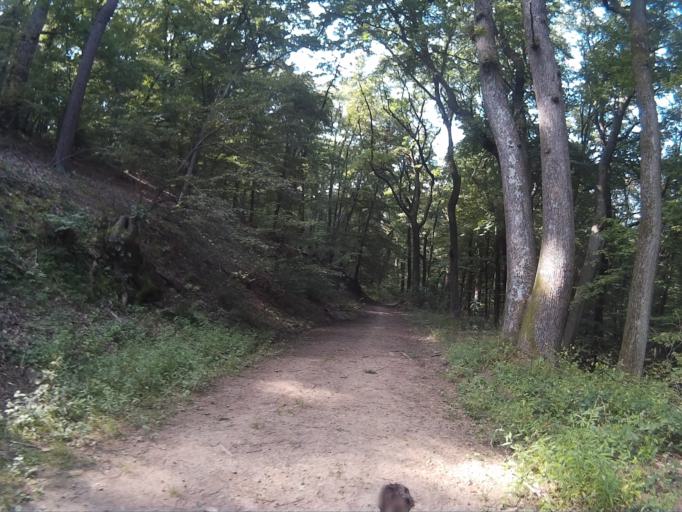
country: AT
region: Burgenland
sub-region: Politischer Bezirk Oberpullendorf
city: Mannersdorf an der Rabnitz
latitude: 47.4044
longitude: 16.5198
